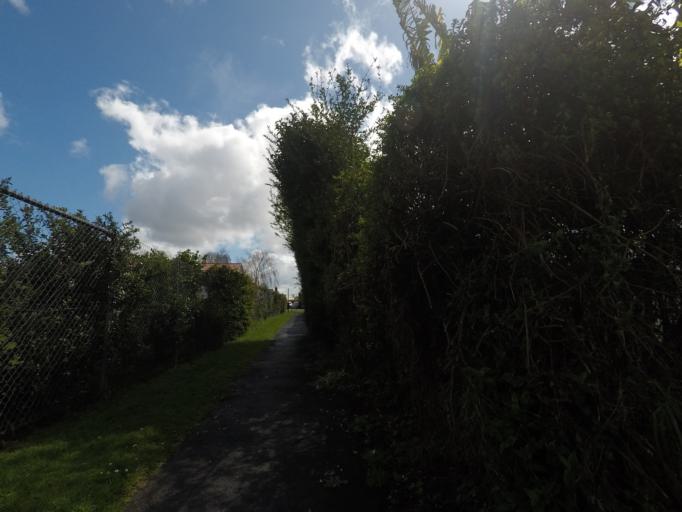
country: NZ
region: Auckland
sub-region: Auckland
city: Rosebank
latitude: -36.8899
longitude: 174.6805
